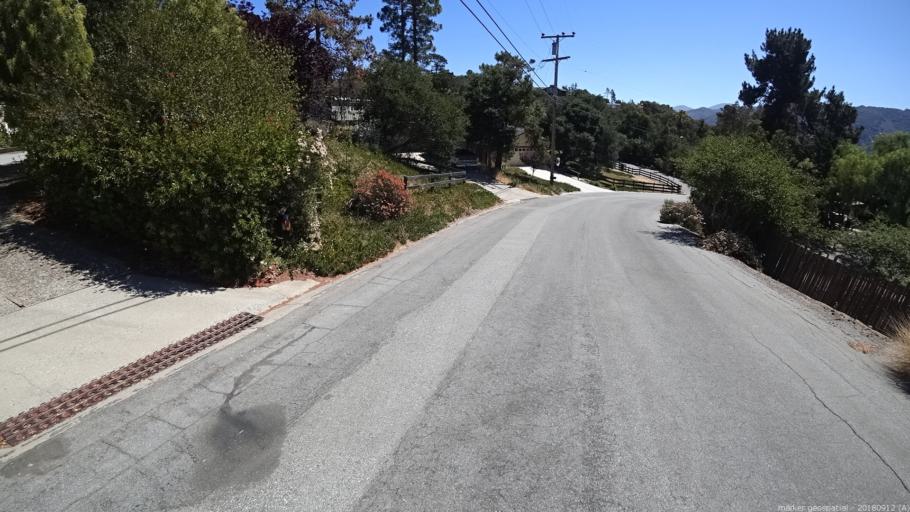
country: US
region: California
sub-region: Monterey County
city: Carmel Valley Village
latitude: 36.4933
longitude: -121.7383
